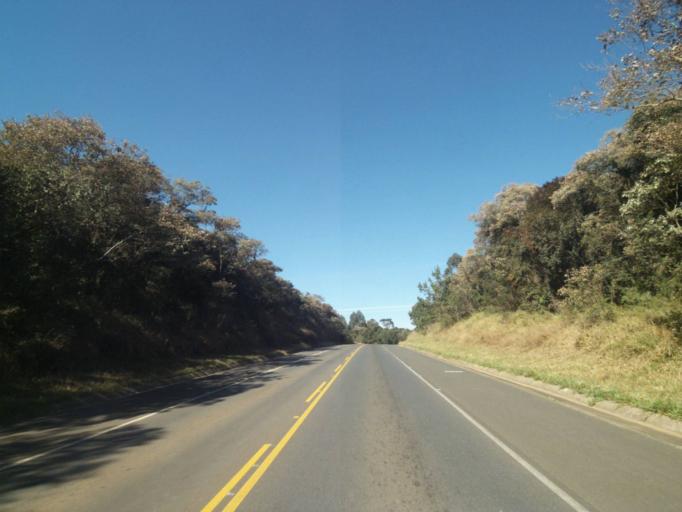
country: BR
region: Parana
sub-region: Tibagi
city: Tibagi
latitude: -24.5573
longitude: -50.4554
